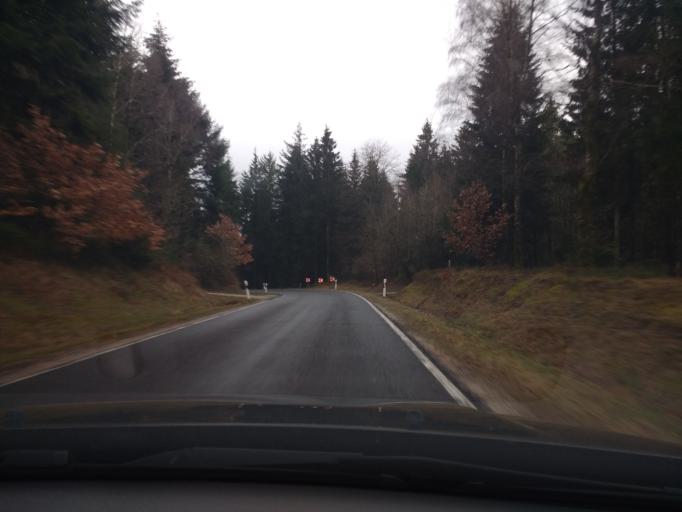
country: DE
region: Rheinland-Pfalz
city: Damflos
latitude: 49.6623
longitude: 6.9916
